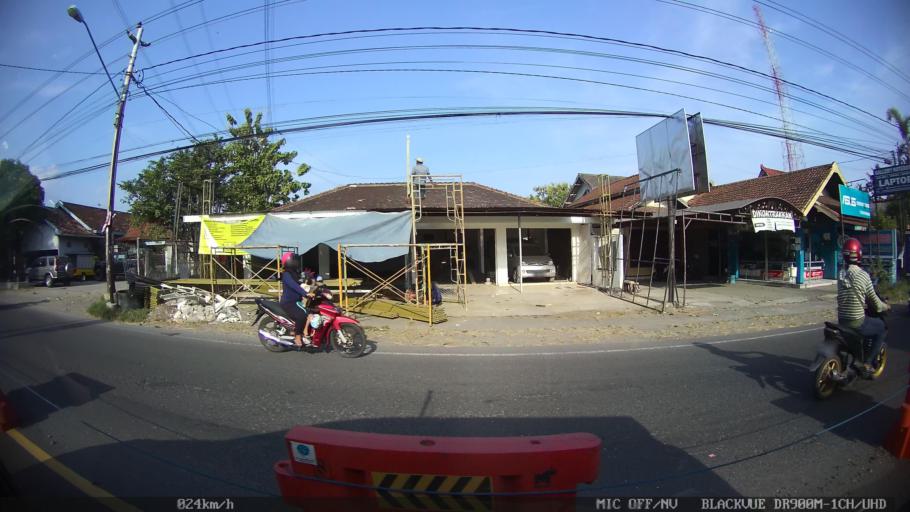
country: ID
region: Daerah Istimewa Yogyakarta
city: Bantul
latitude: -7.8696
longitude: 110.3374
